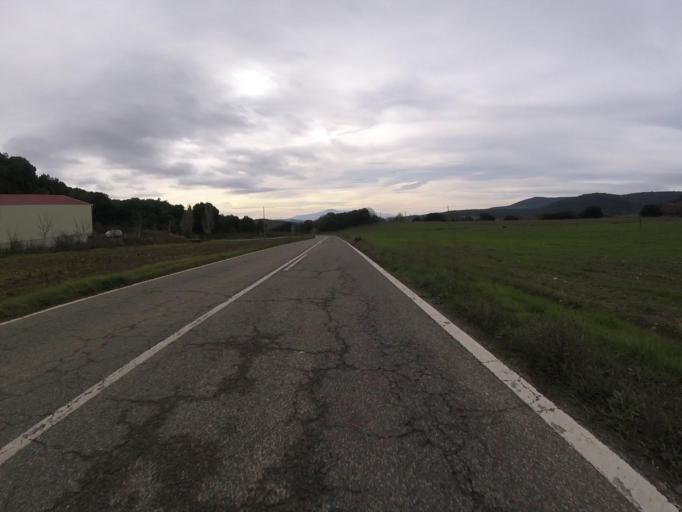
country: ES
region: Navarre
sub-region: Provincia de Navarra
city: Lezaun
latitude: 42.7455
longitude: -2.0205
